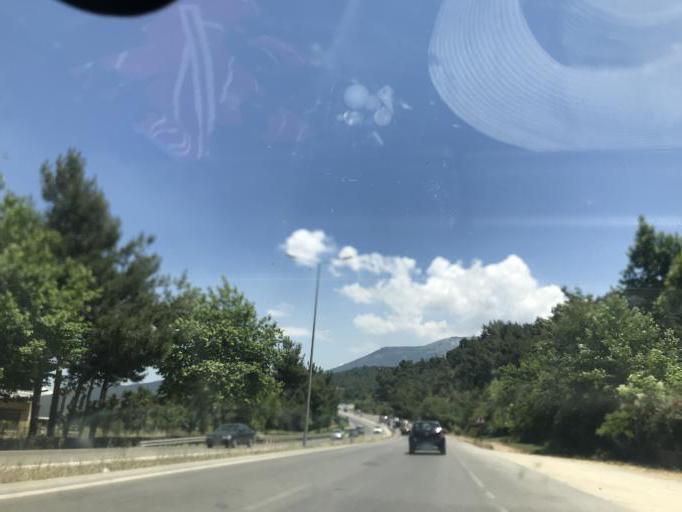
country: TR
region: Denizli
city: Denizli
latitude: 37.7312
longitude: 29.1592
